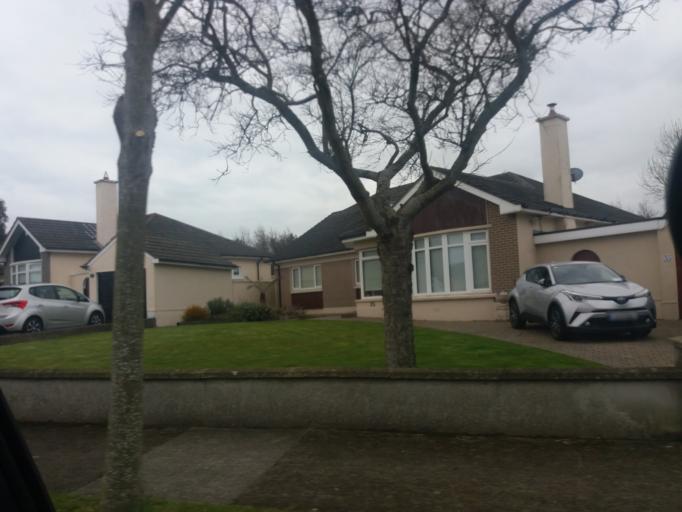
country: IE
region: Leinster
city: Sutton
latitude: 53.3838
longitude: -6.0929
